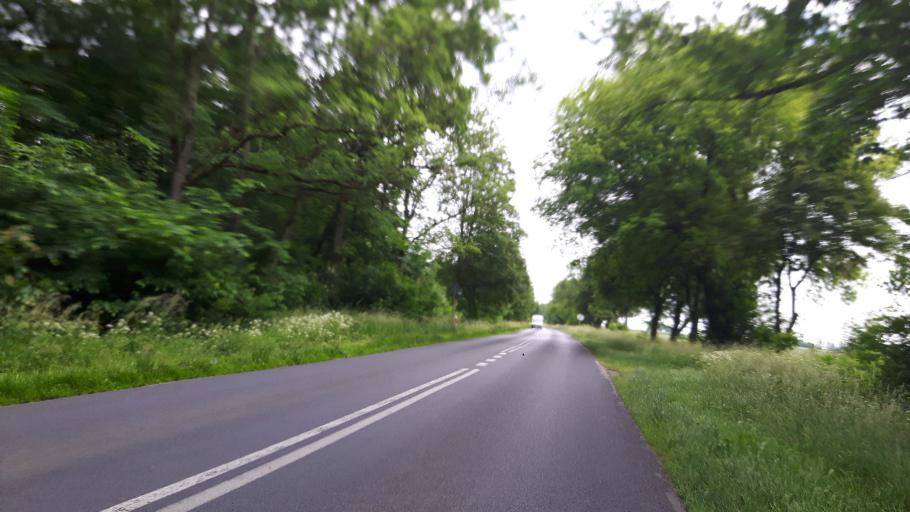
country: PL
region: West Pomeranian Voivodeship
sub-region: Powiat gryficki
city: Gryfice
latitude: 53.9454
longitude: 15.2229
